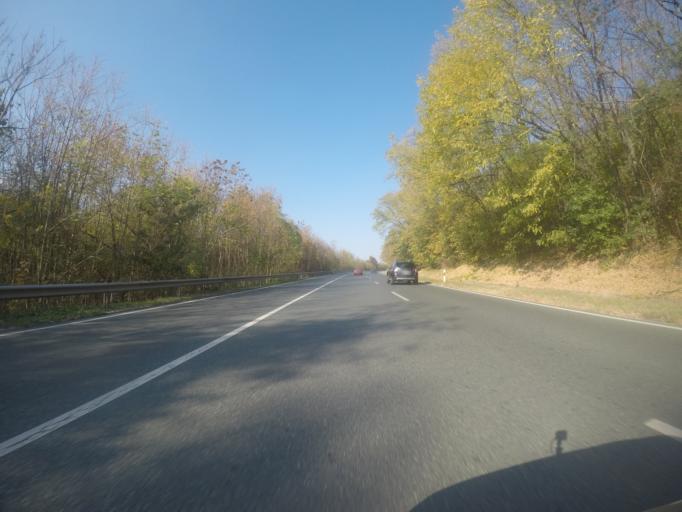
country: HU
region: Tolna
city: Madocsa
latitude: 46.6925
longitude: 18.8867
